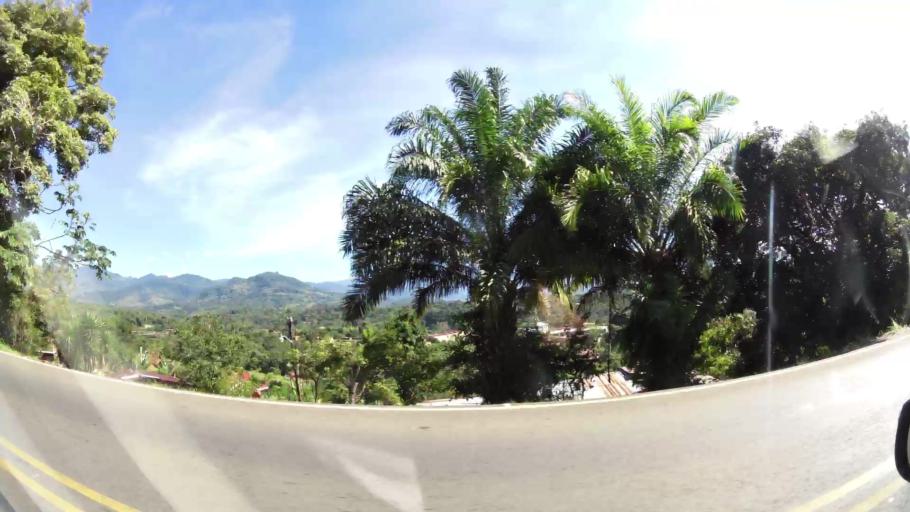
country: CR
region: San Jose
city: San Isidro
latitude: 9.3911
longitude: -83.7074
